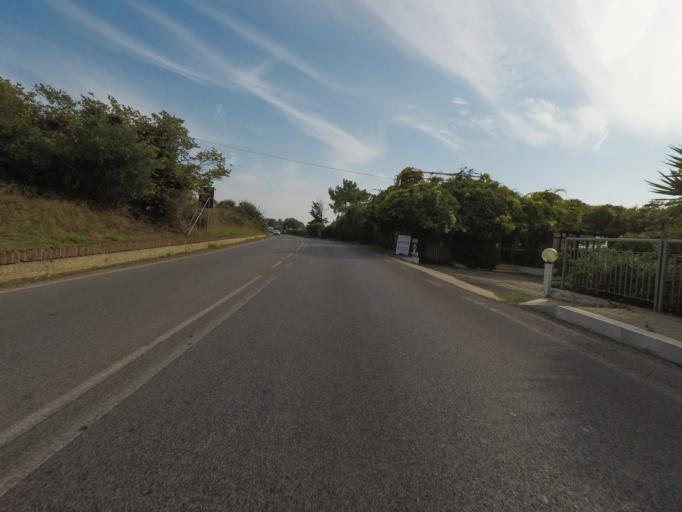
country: IT
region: Latium
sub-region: Citta metropolitana di Roma Capitale
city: Civitavecchia
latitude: 42.0643
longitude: 11.8141
